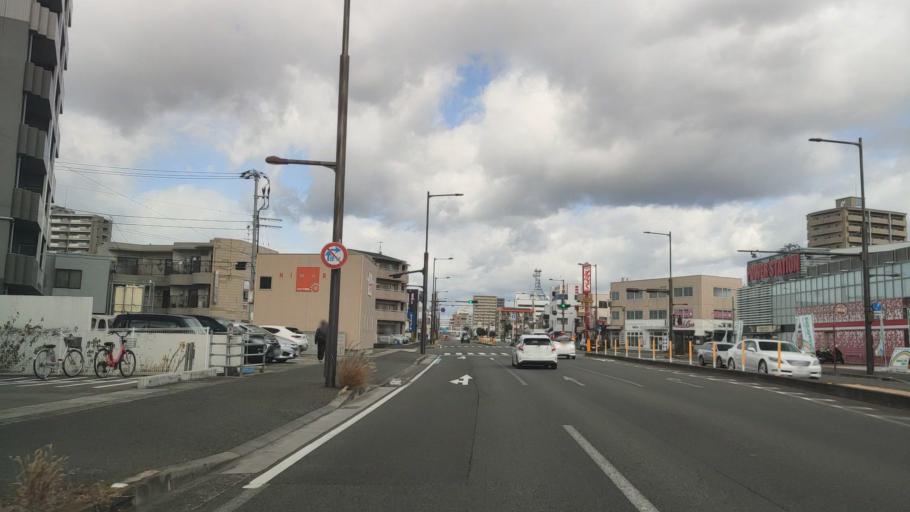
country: JP
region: Ehime
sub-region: Shikoku-chuo Shi
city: Matsuyama
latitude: 33.8273
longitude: 132.7588
